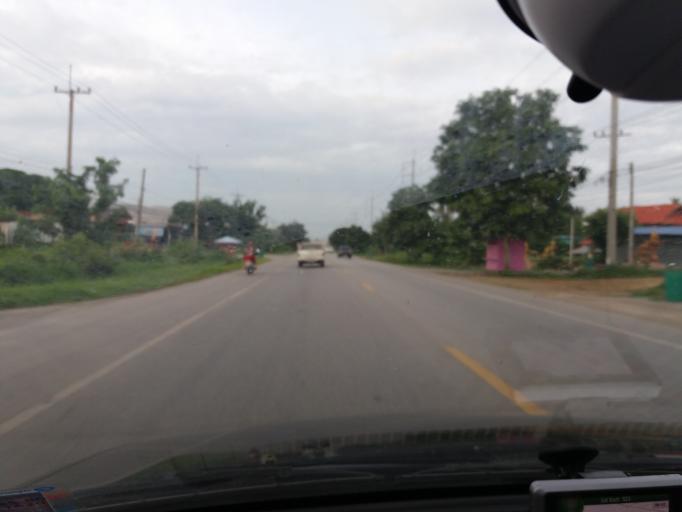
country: TH
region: Suphan Buri
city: U Thong
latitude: 14.4106
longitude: 99.9006
